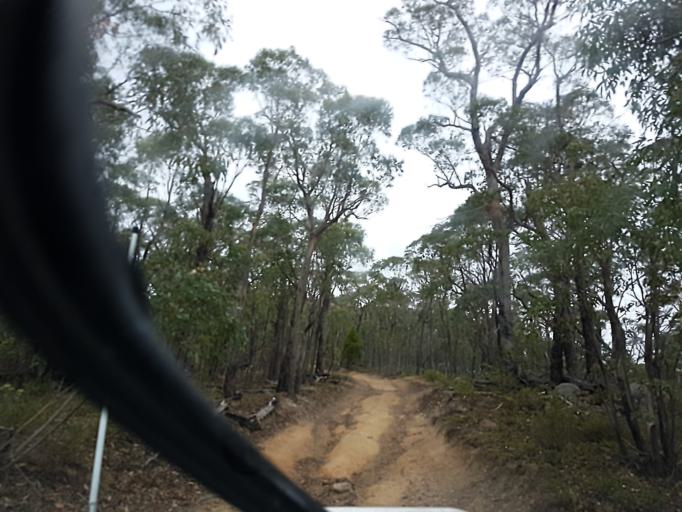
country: AU
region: New South Wales
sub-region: Snowy River
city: Jindabyne
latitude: -36.8729
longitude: 148.3309
